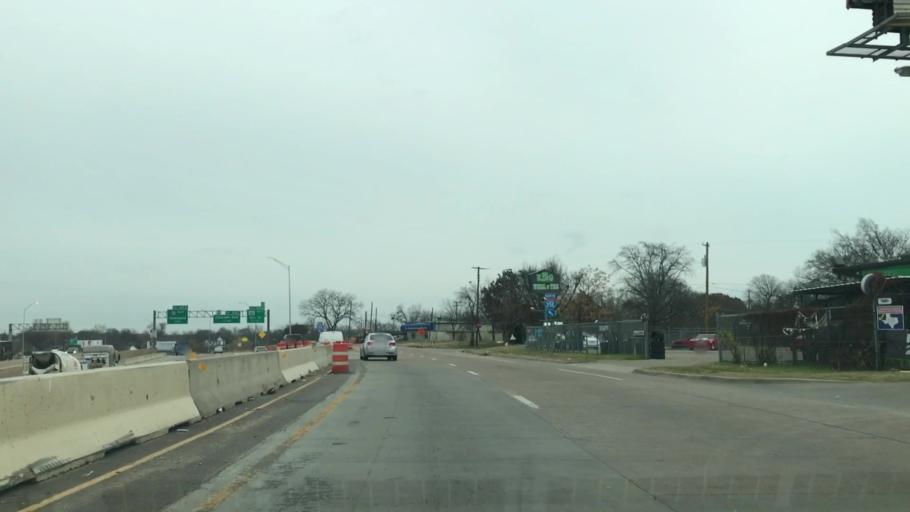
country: US
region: Texas
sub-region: Dallas County
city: Dallas
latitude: 32.7454
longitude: -96.8119
